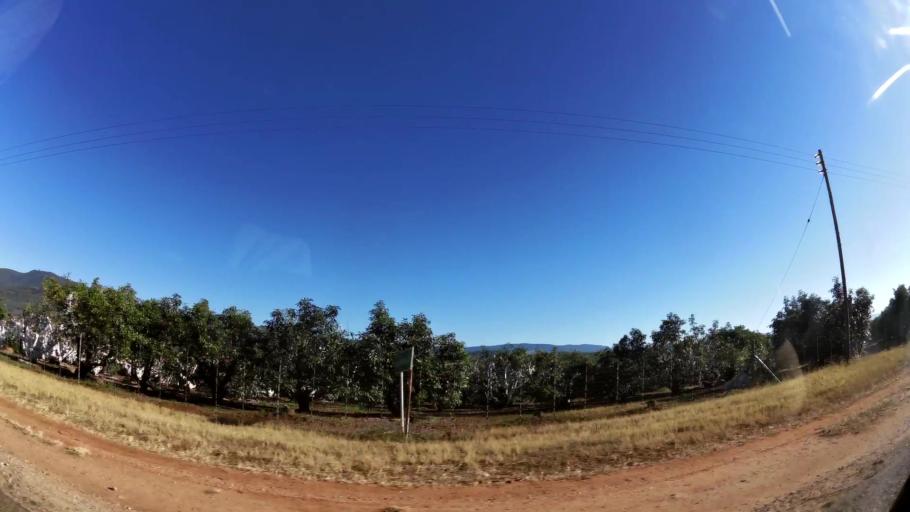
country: ZA
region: Limpopo
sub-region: Mopani District Municipality
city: Tzaneen
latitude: -23.8484
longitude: 30.1188
